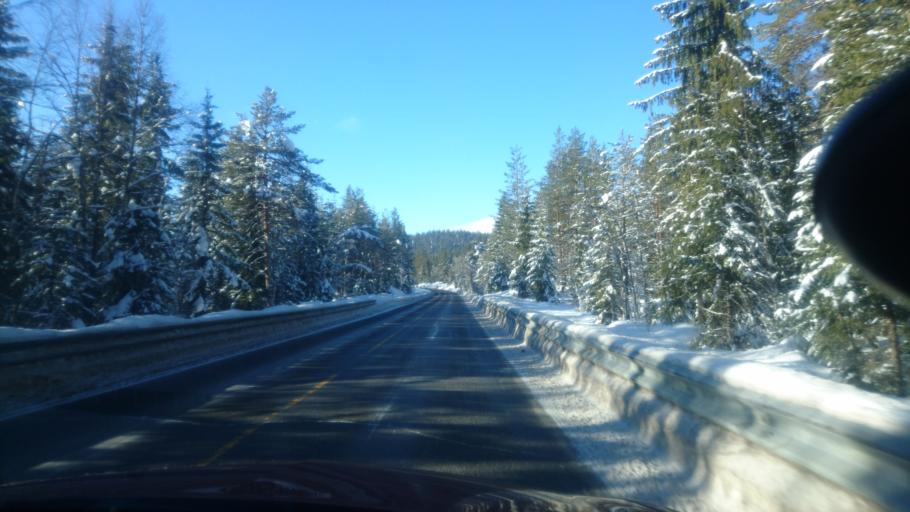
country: NO
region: Hedmark
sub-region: Trysil
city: Innbygda
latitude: 61.2654
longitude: 12.3724
